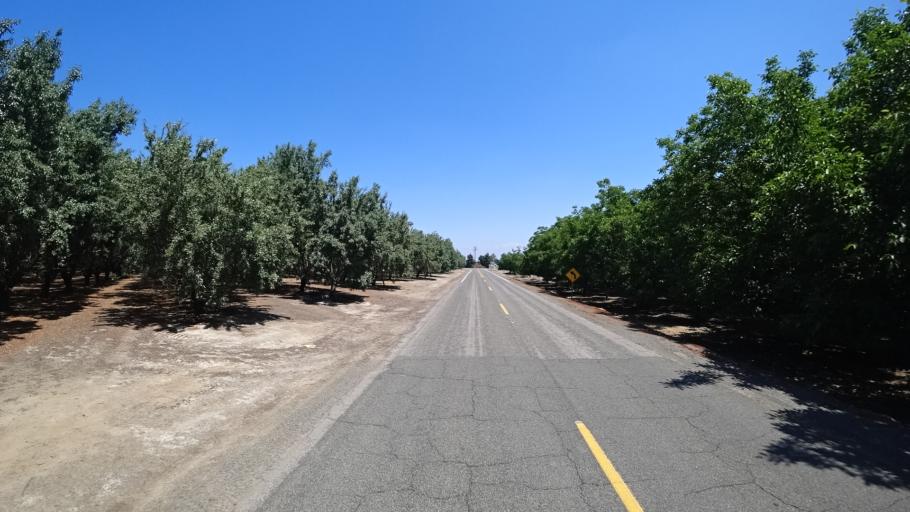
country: US
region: California
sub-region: Fresno County
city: Kingsburg
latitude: 36.4841
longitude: -119.5653
